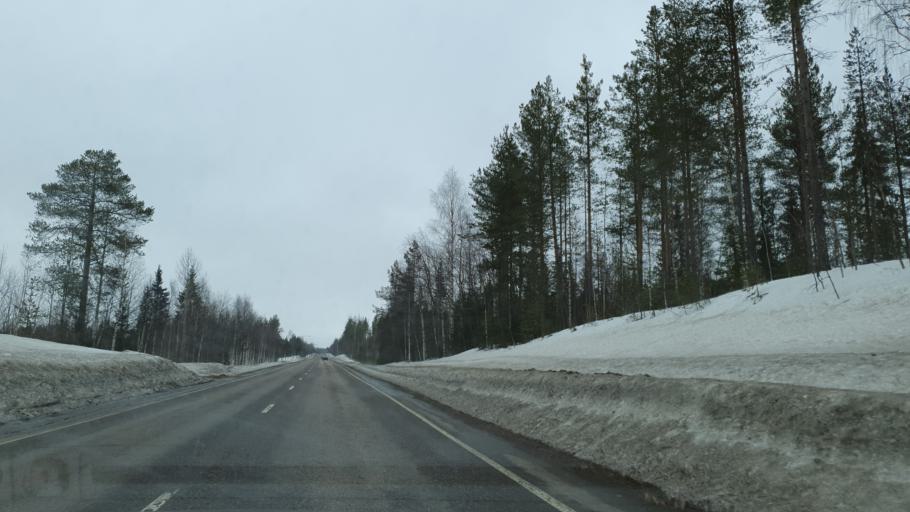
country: FI
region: Lapland
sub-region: Torniolaakso
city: Pello
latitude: 66.8780
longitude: 24.0653
